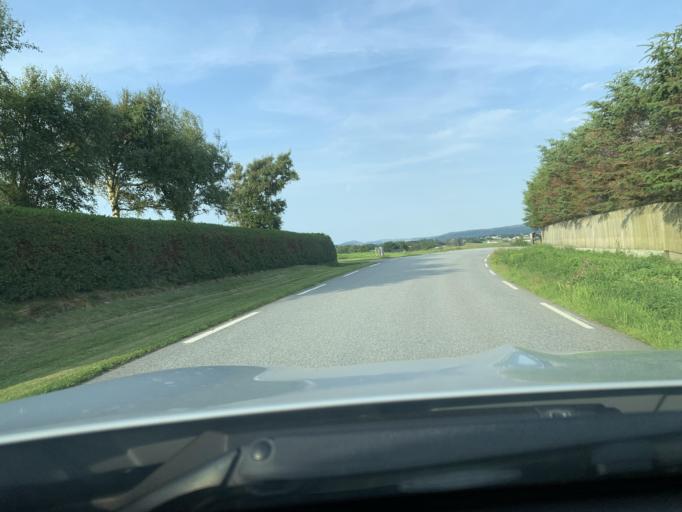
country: NO
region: Rogaland
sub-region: Time
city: Bryne
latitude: 58.7329
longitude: 5.5942
